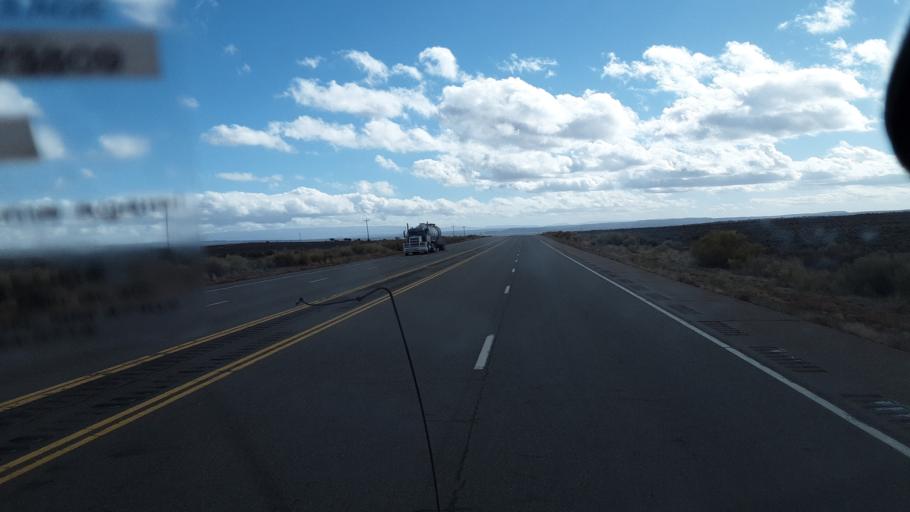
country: US
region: New Mexico
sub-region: Rio Arriba County
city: Santa Teresa
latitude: 36.1933
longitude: -107.3894
